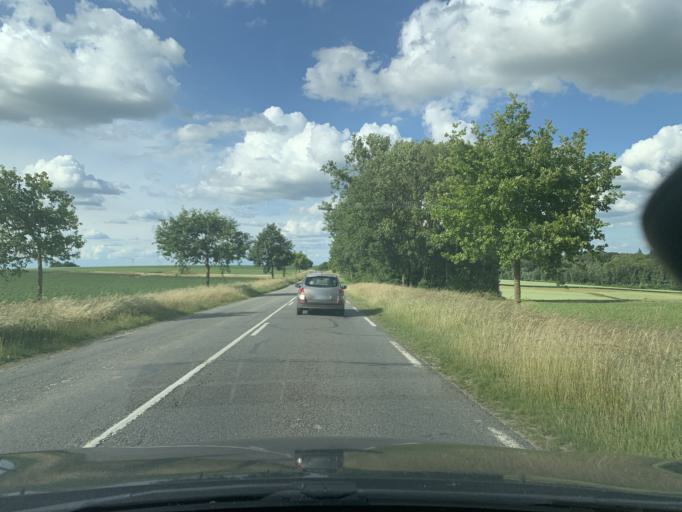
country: FR
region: Picardie
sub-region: Departement de la Somme
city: Moislains
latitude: 49.9685
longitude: 2.9882
